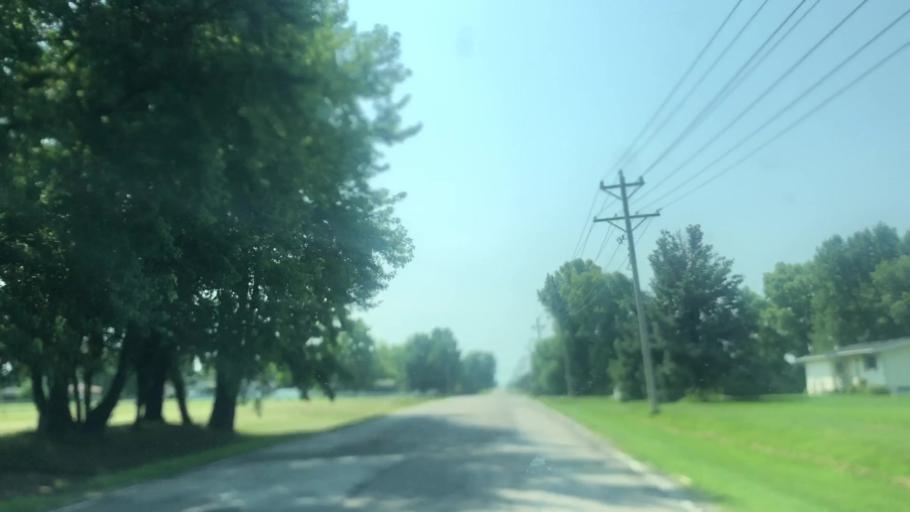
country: US
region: Iowa
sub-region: Marshall County
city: Marshalltown
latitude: 42.0445
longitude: -92.9611
